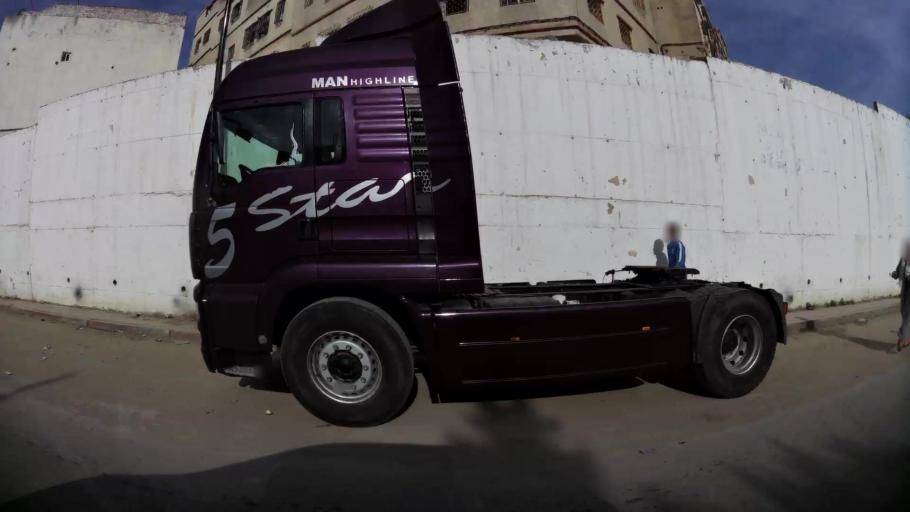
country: MA
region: Tanger-Tetouan
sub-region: Tanger-Assilah
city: Tangier
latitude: 35.7610
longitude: -5.7835
